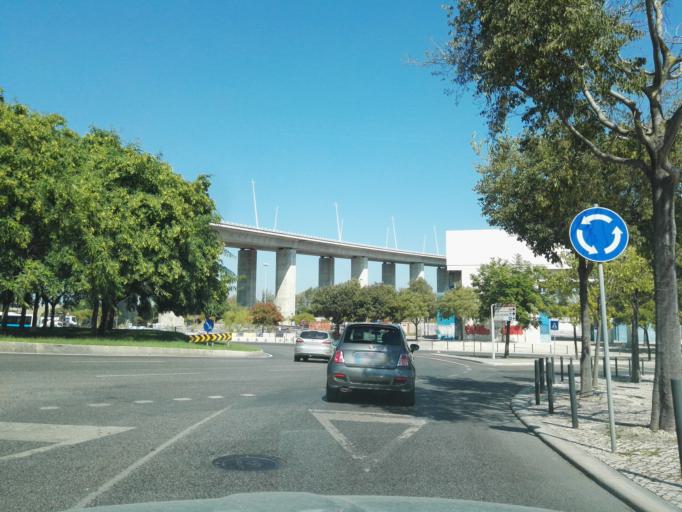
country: PT
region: Lisbon
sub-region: Loures
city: Moscavide
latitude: 38.7854
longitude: -9.0999
